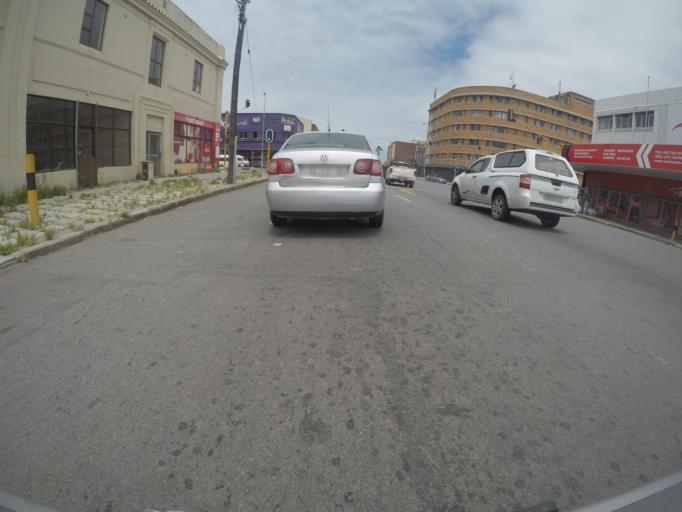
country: ZA
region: Eastern Cape
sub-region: Buffalo City Metropolitan Municipality
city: East London
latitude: -33.0172
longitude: 27.9130
